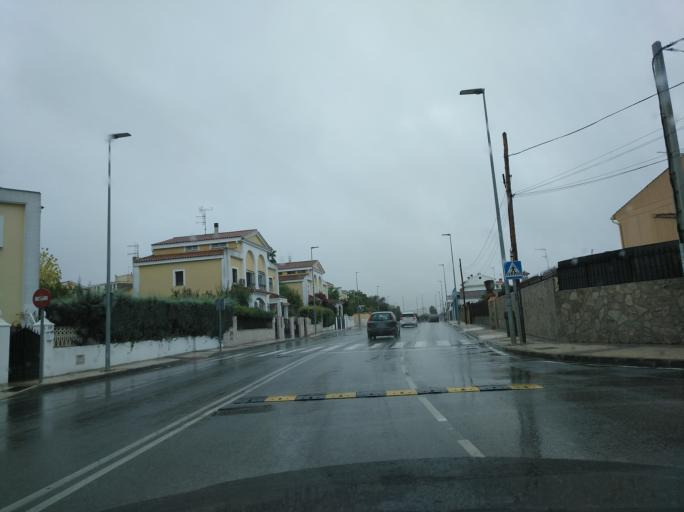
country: ES
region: Extremadura
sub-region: Provincia de Badajoz
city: Badajoz
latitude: 38.8878
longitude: -6.9911
